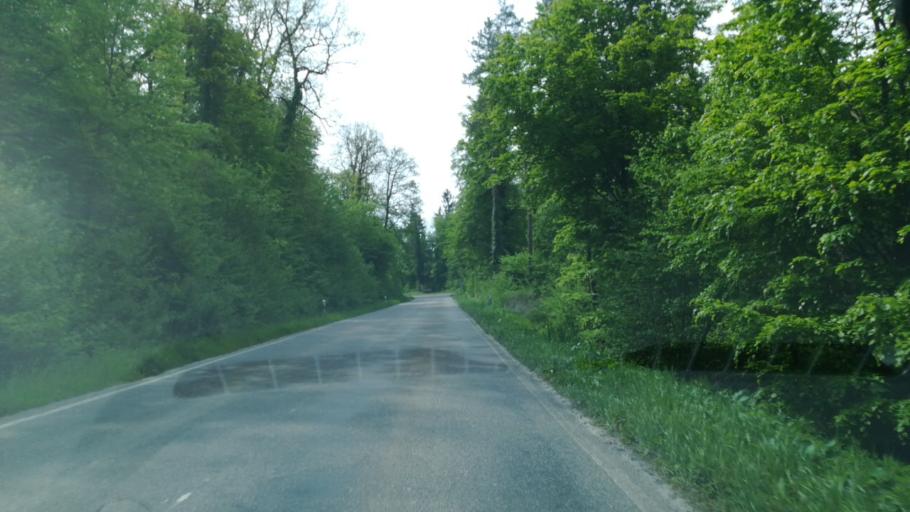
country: DE
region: Baden-Wuerttemberg
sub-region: Freiburg Region
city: Steisslingen
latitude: 47.7668
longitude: 8.8934
